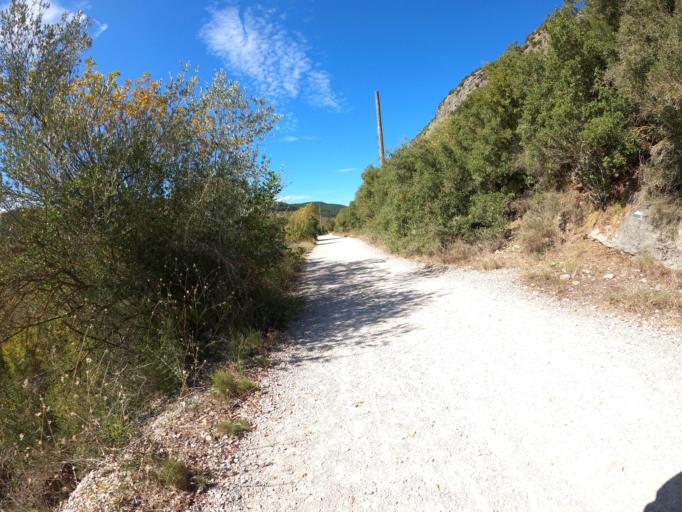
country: ES
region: Navarre
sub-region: Provincia de Navarra
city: Liedena
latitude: 42.6242
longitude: -1.2968
